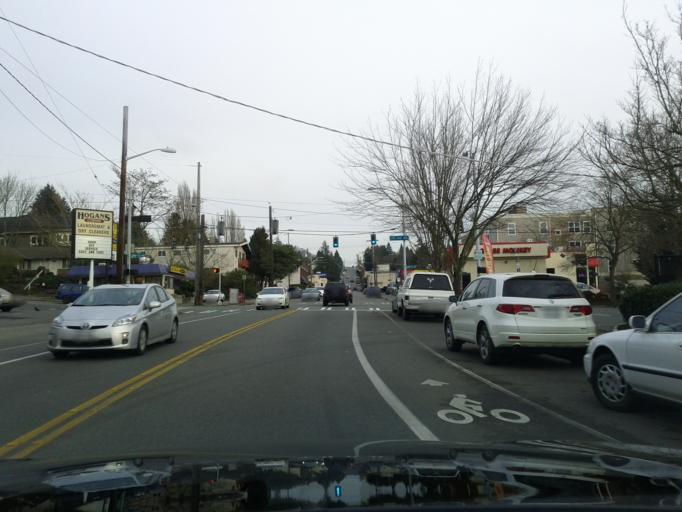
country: US
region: Washington
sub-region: King County
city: Seattle
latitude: 47.6685
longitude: -122.3013
